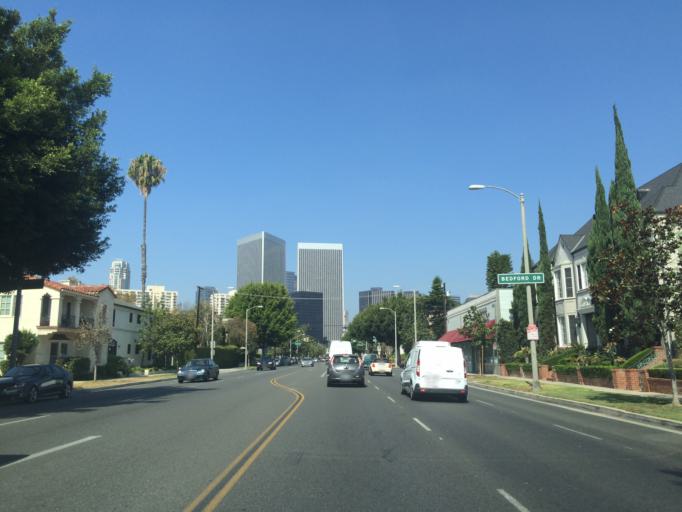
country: US
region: California
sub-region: Los Angeles County
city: Beverly Hills
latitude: 34.0598
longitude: -118.4036
